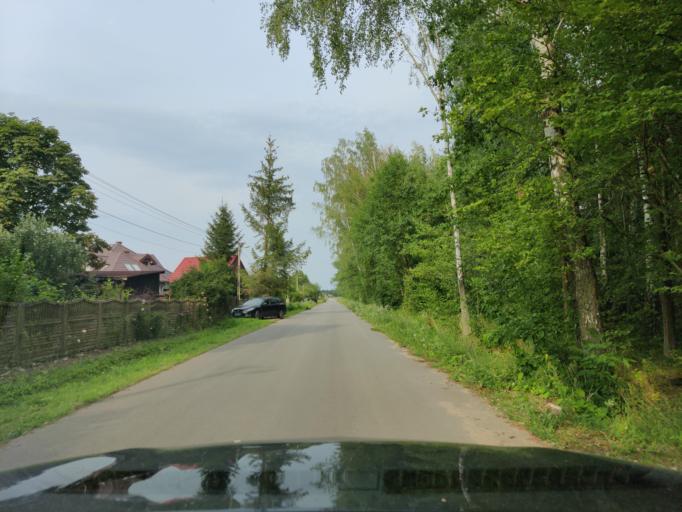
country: PL
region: Masovian Voivodeship
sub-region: Powiat pultuski
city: Obryte
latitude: 52.7060
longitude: 21.2277
